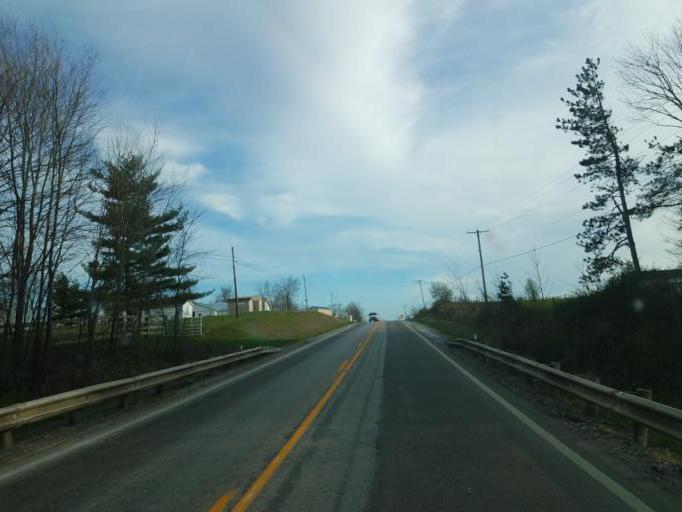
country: US
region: Ohio
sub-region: Richland County
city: Lexington
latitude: 40.6052
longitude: -82.6625
